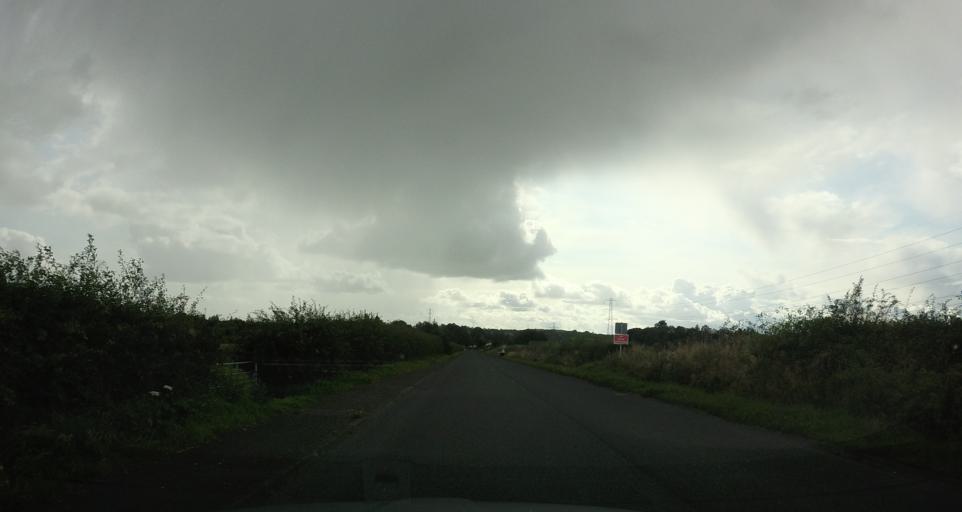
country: GB
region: Scotland
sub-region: Clackmannanshire
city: Dollar
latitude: 56.1509
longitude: -3.6398
